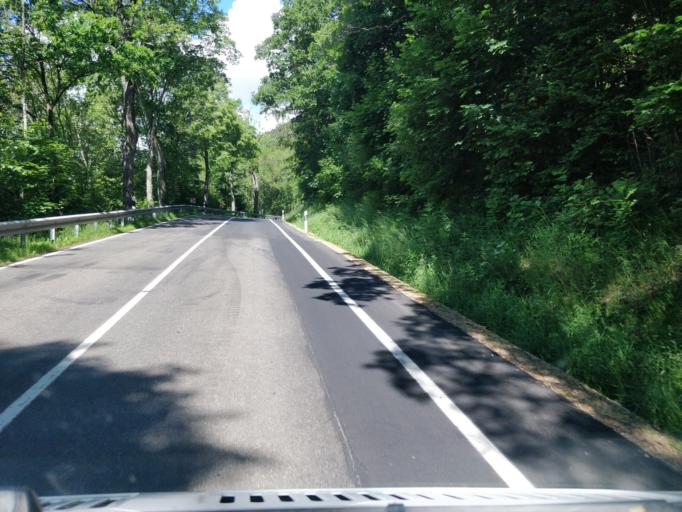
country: DE
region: Rheinland-Pfalz
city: Ormont
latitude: 50.3617
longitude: 6.4652
